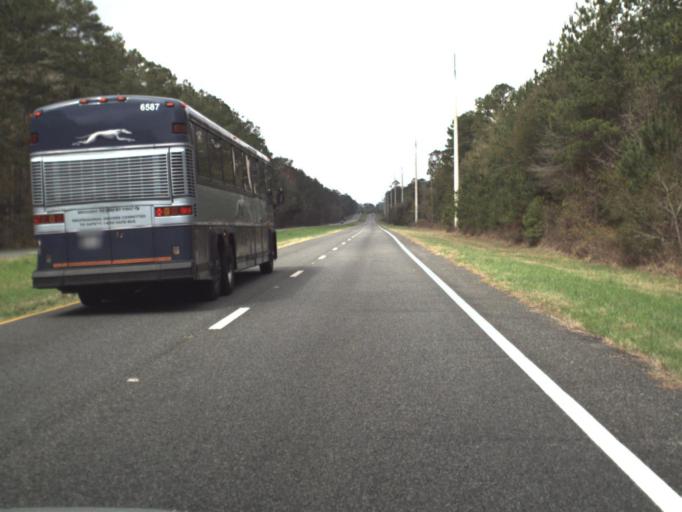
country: US
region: Florida
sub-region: Leon County
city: Woodville
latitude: 30.4042
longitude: -84.0564
